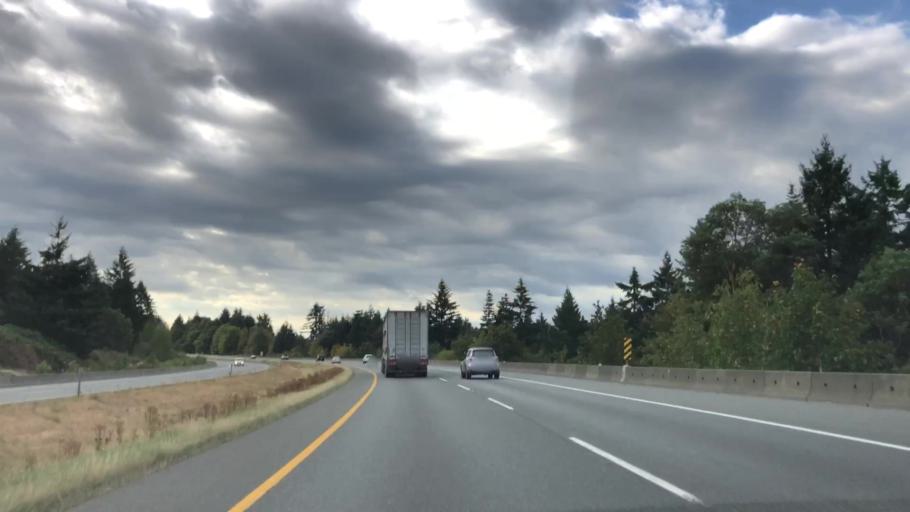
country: CA
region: British Columbia
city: Nanaimo
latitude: 49.1985
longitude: -124.0272
